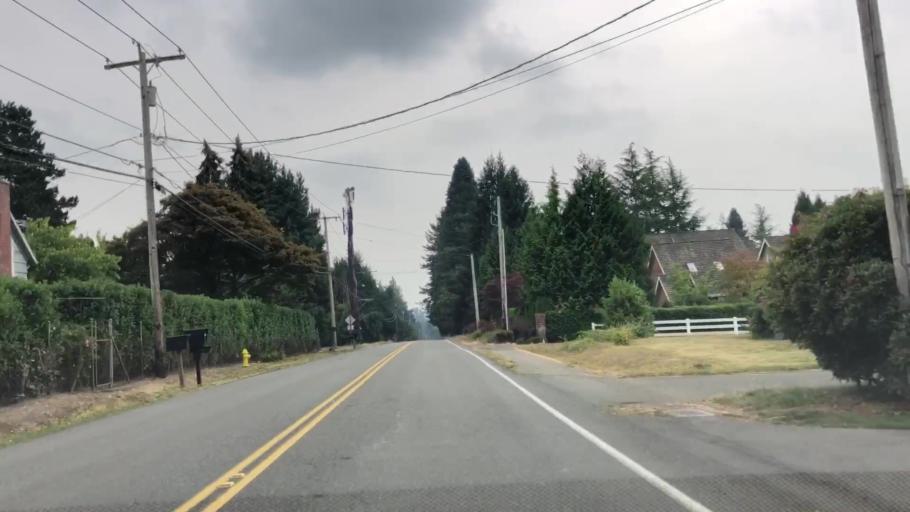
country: US
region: Washington
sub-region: King County
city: Cottage Lake
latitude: 47.7359
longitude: -122.1153
